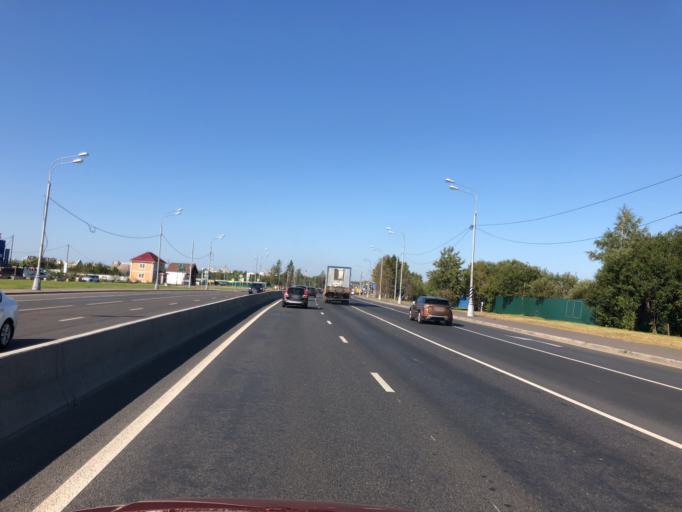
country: RU
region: Moskovskaya
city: Troitsk
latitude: 55.4498
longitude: 37.2908
